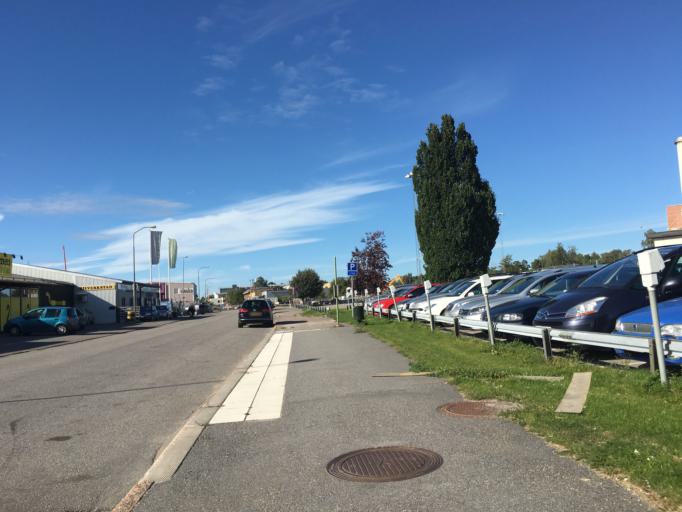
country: SE
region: Uppsala
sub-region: Uppsala Kommun
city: Uppsala
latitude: 59.8502
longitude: 17.6731
